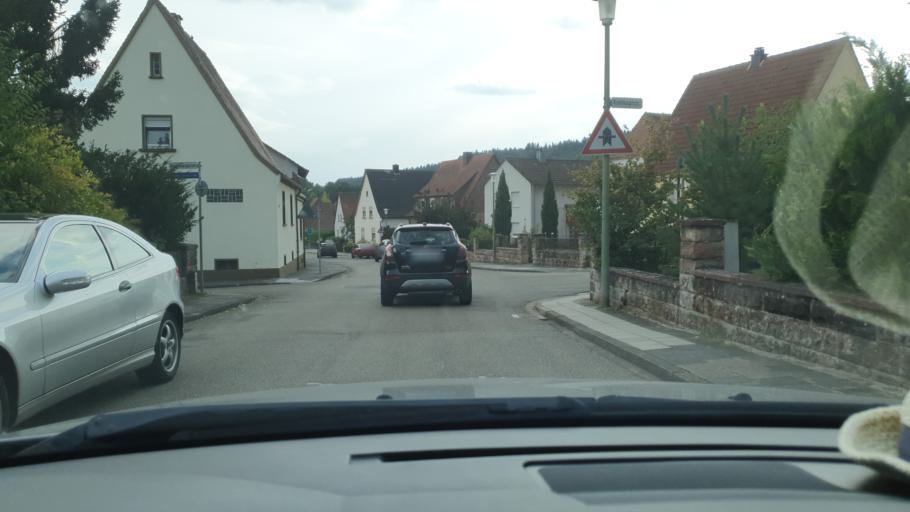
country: DE
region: Rheinland-Pfalz
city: Stelzenberg
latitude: 49.4200
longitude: 7.6977
